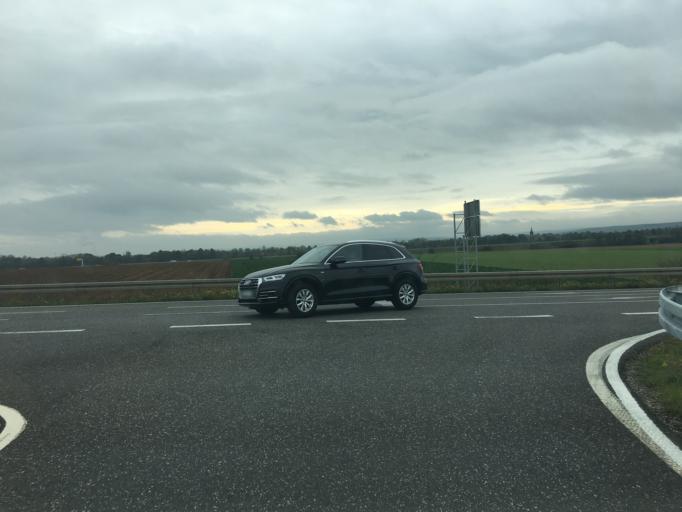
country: DE
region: North Rhine-Westphalia
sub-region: Regierungsbezirk Koln
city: Euskirchen
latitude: 50.6769
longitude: 6.7310
